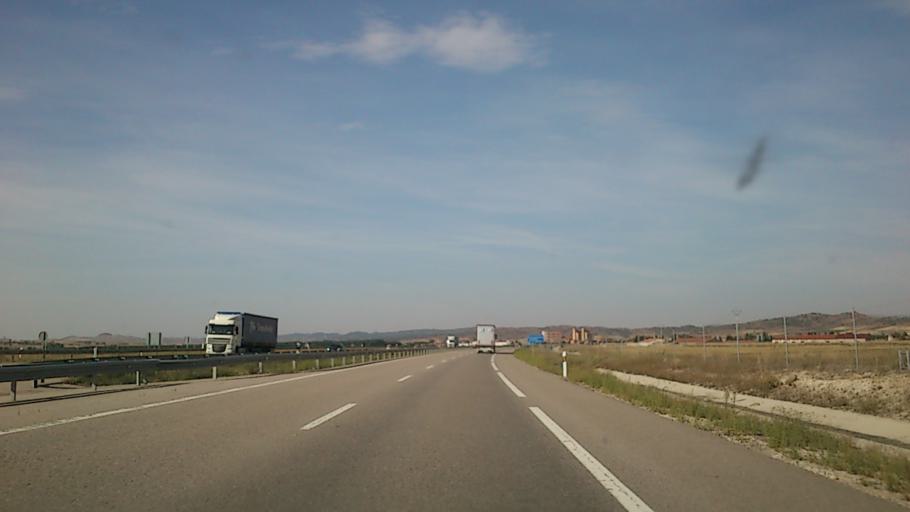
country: ES
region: Aragon
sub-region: Provincia de Teruel
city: Fuentes Claras
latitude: 40.8891
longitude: -1.3056
